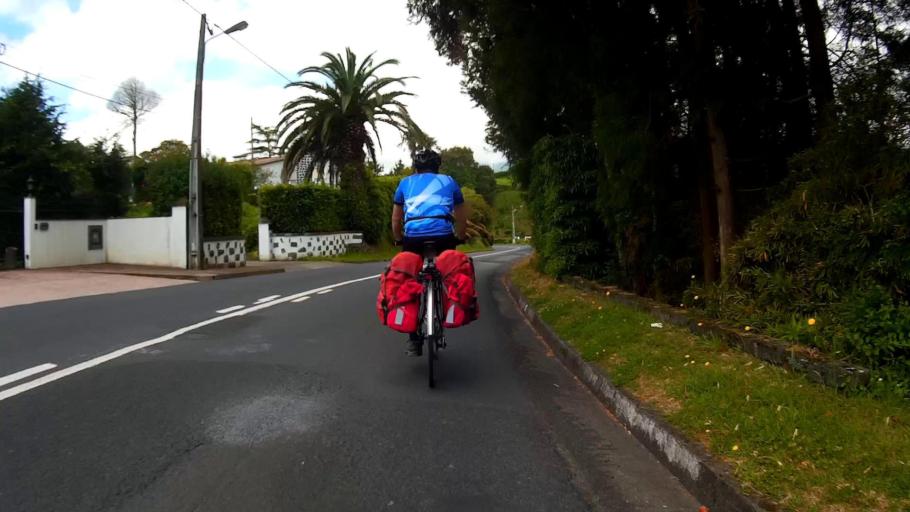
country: PT
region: Azores
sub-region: Povoacao
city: Furnas
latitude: 37.7725
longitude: -25.3024
